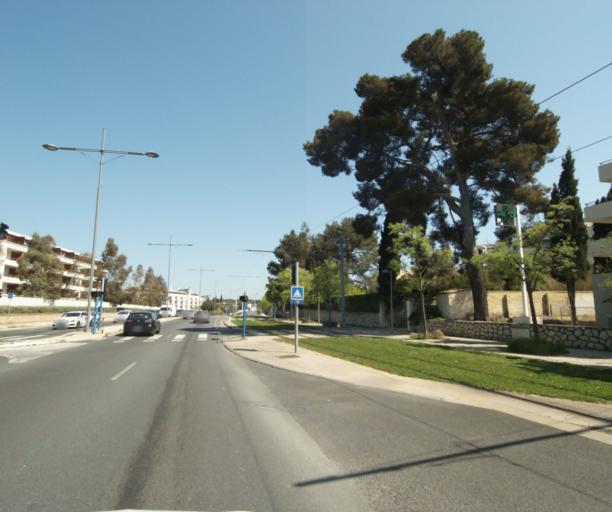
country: FR
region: Languedoc-Roussillon
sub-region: Departement de l'Herault
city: Montferrier-sur-Lez
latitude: 43.6337
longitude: 3.8433
